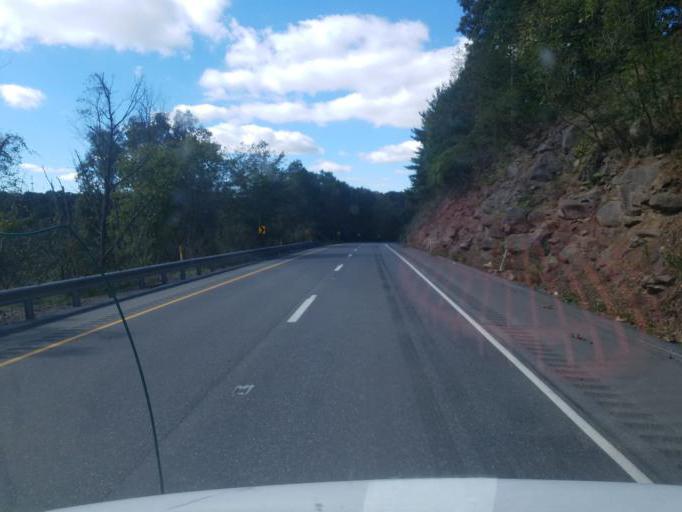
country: US
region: Pennsylvania
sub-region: Bedford County
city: Earlston
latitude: 39.9968
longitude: -78.2570
